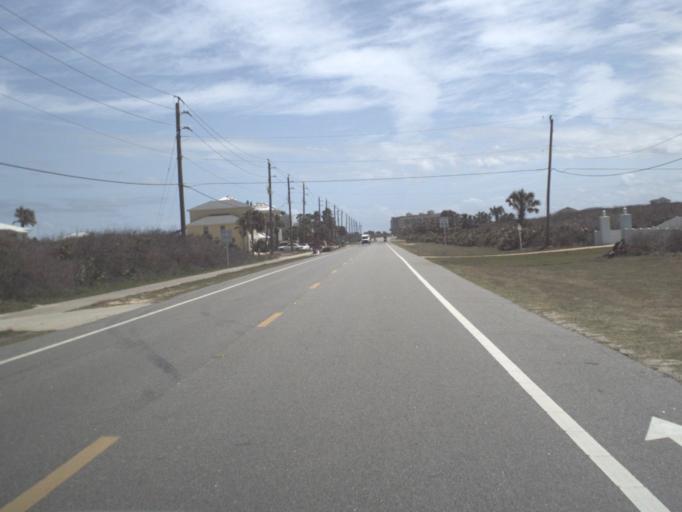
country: US
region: Florida
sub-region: Flagler County
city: Palm Coast
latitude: 29.6603
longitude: -81.2098
